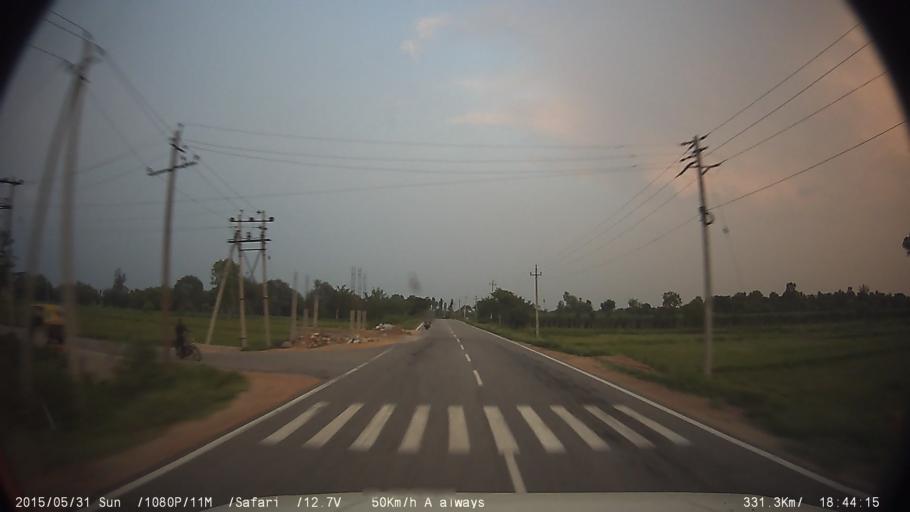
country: IN
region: Karnataka
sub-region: Mysore
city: Tirumakudal Narsipur
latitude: 12.1569
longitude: 76.8140
